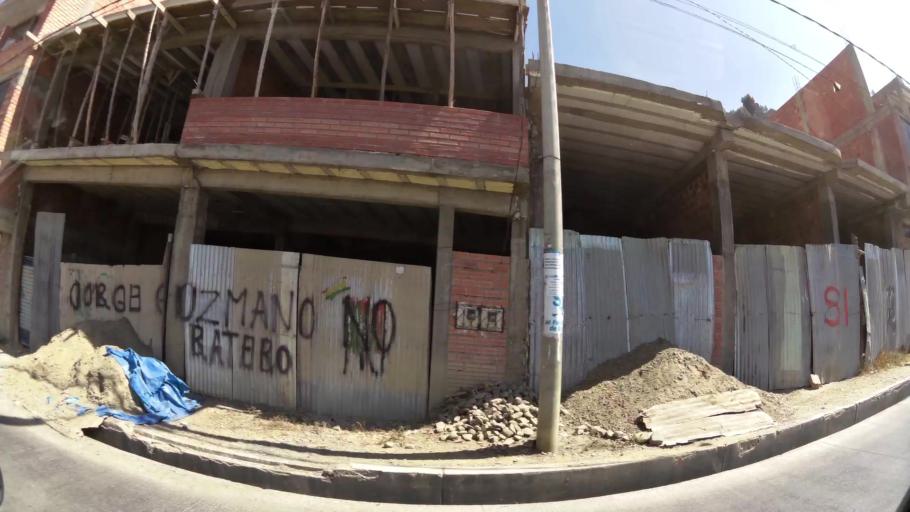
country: BO
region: La Paz
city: La Paz
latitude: -16.5329
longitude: -68.1460
